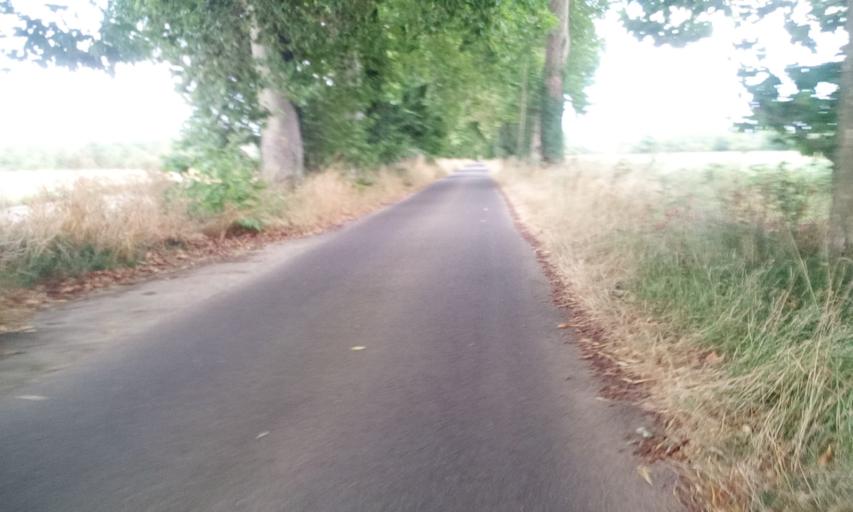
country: FR
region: Lower Normandy
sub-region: Departement du Calvados
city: Bellengreville
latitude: 49.1443
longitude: -0.2070
